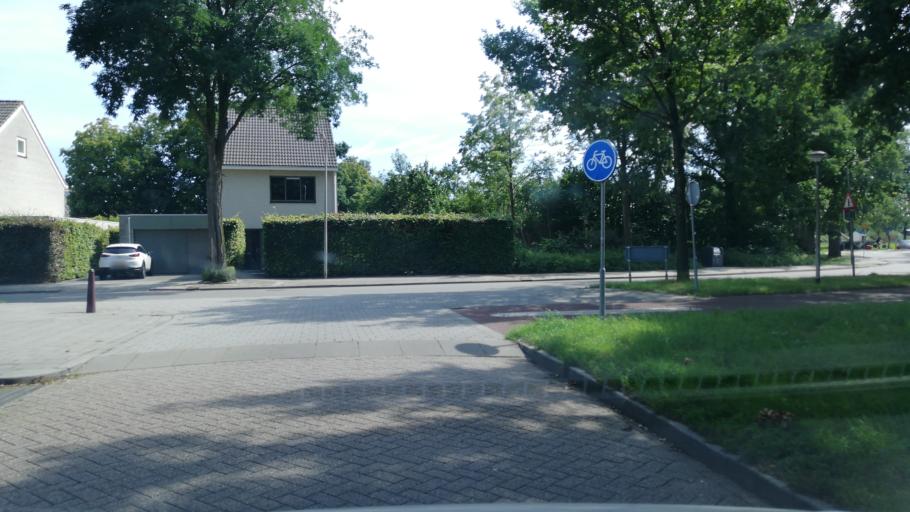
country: NL
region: Overijssel
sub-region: Gemeente Zwolle
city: Zwolle
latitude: 52.4939
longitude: 6.1047
